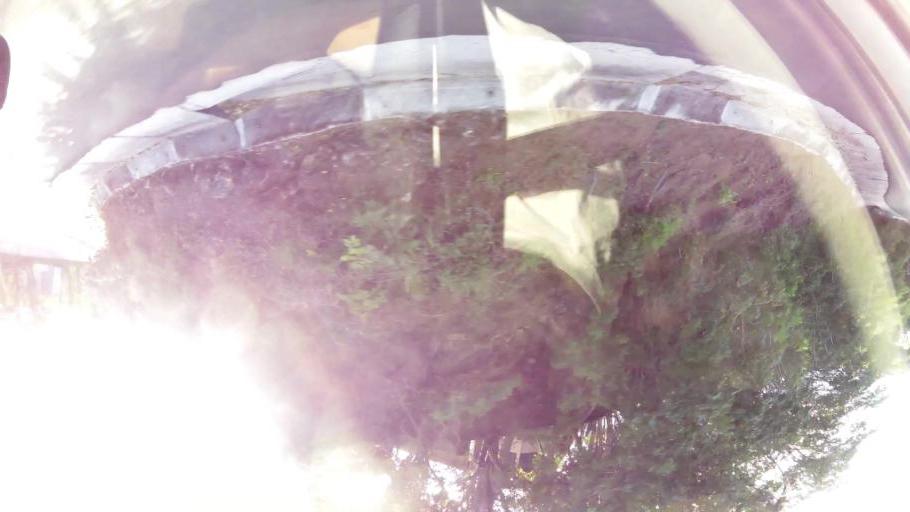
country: CR
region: Guanacaste
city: Sardinal
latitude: 10.5663
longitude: -85.6808
